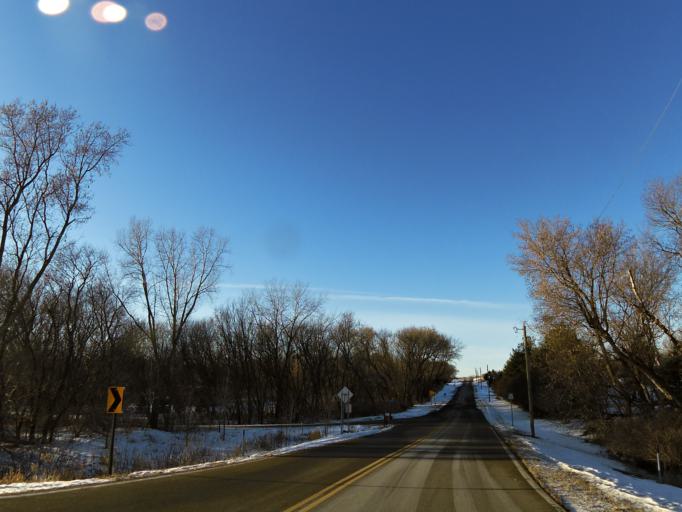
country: US
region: Minnesota
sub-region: Dakota County
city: Hastings
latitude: 44.7937
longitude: -92.8635
